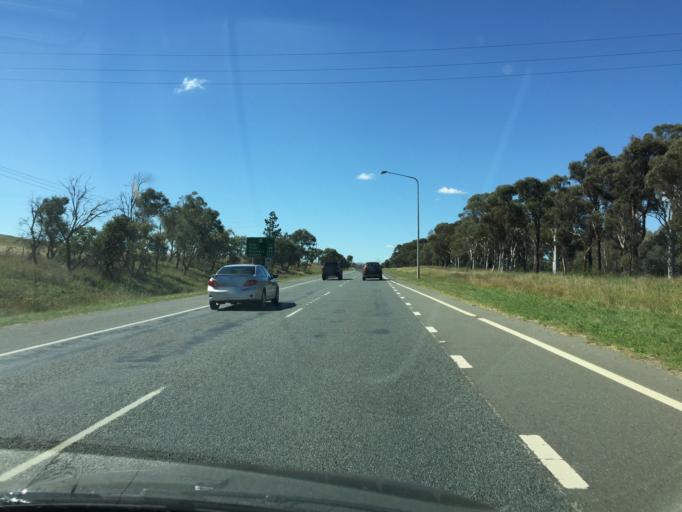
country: AU
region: Australian Capital Territory
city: Macarthur
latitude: -35.3797
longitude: 149.1697
